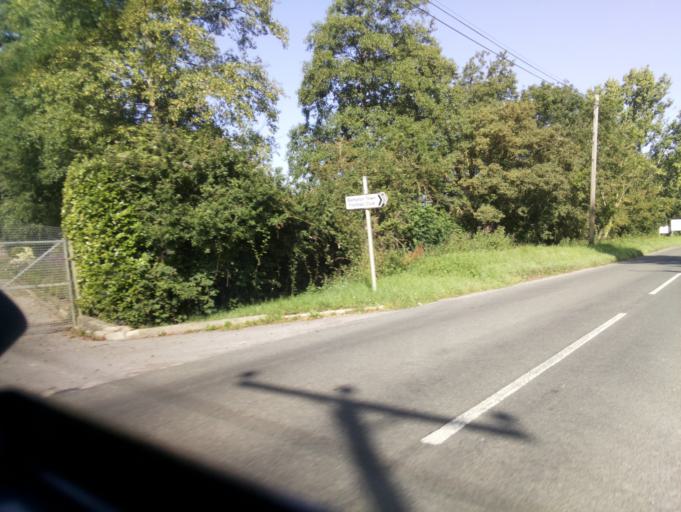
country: GB
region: England
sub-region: Oxfordshire
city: Bampton
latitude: 51.7197
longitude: -1.5328
